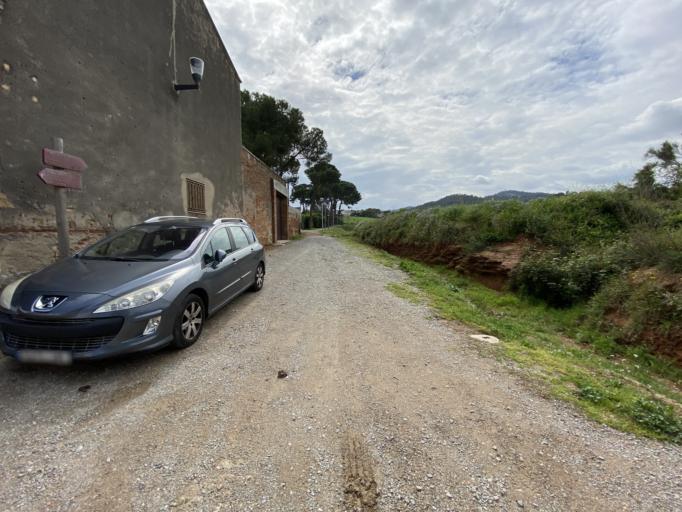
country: ES
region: Catalonia
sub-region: Provincia de Barcelona
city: Santa Coloma de Cervello
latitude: 41.3612
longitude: 2.0264
